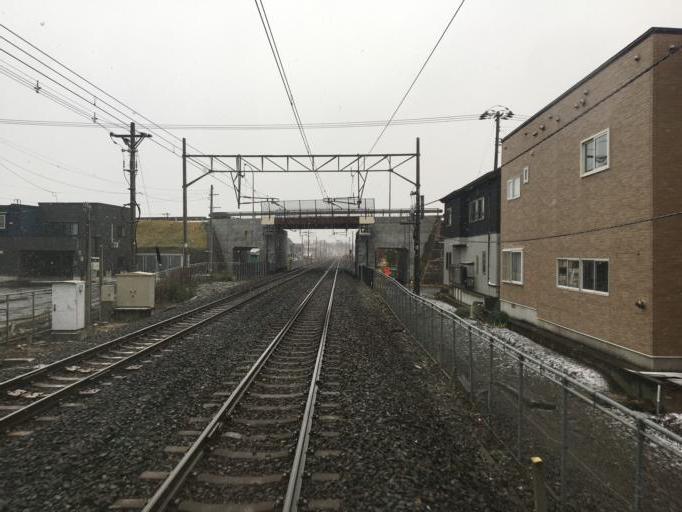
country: JP
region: Aomori
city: Aomori Shi
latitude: 40.8331
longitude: 140.8069
